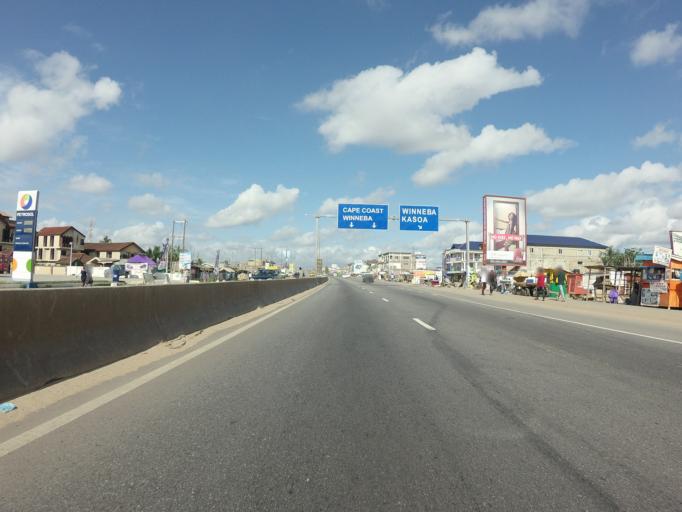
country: GH
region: Central
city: Kasoa
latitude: 5.5356
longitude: -0.4179
